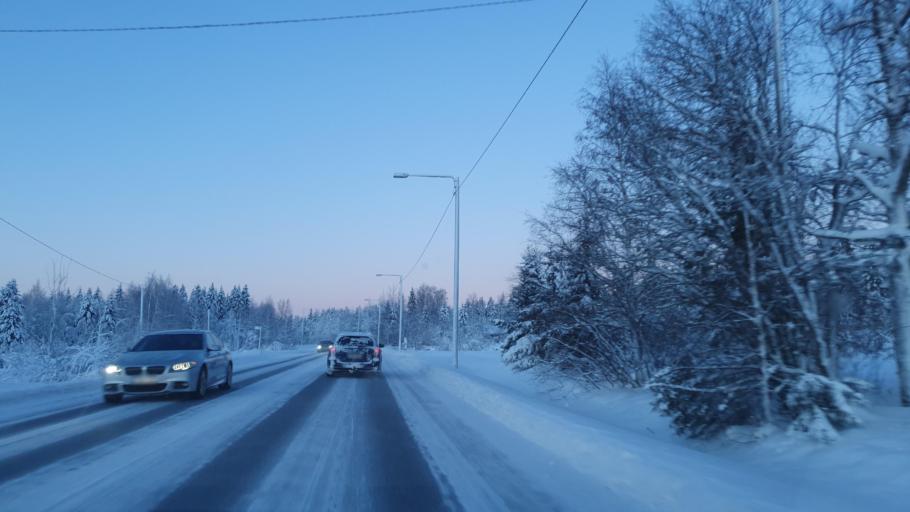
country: FI
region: Lapland
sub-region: Kemi-Tornio
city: Tornio
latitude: 65.9955
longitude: 24.0745
